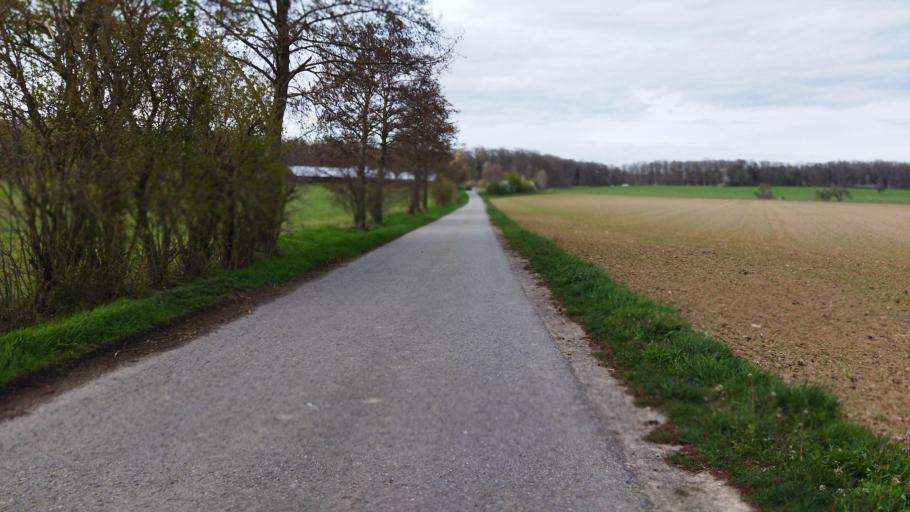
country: DE
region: Baden-Wuerttemberg
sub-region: Regierungsbezirk Stuttgart
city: Gundelsheim
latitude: 49.2953
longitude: 9.1920
